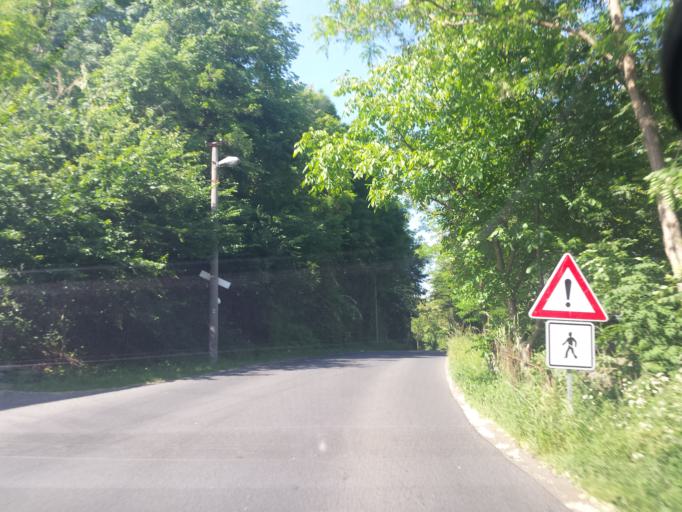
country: CZ
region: Central Bohemia
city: Nelahozeves
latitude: 50.2636
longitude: 14.3022
